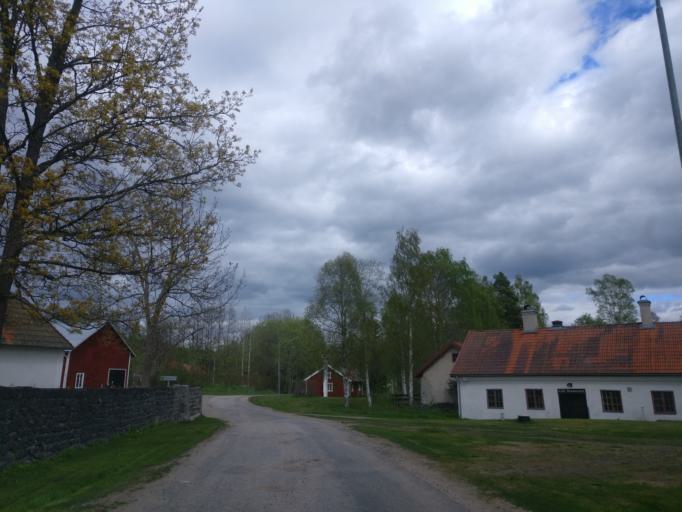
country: SE
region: Gaevleborg
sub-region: Soderhamns Kommun
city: Marielund
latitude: 61.4597
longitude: 17.1243
